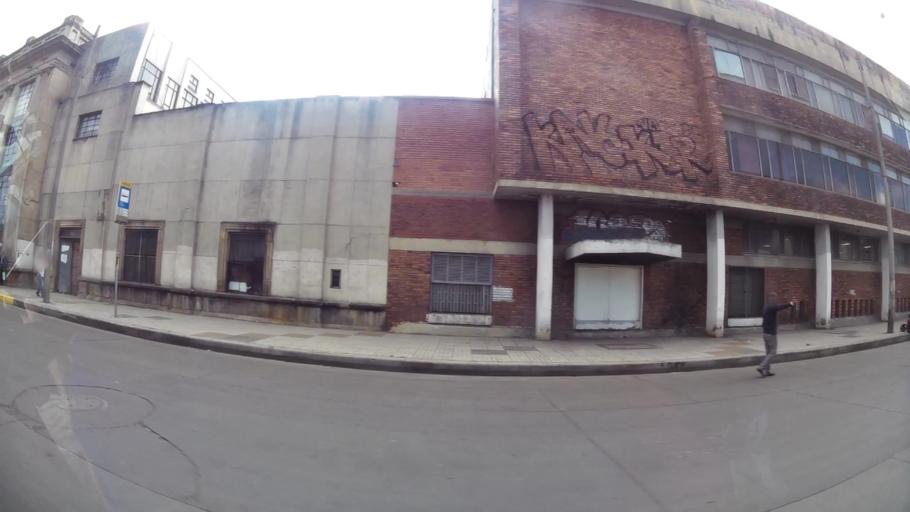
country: CO
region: Bogota D.C.
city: Bogota
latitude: 4.6072
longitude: -74.0828
